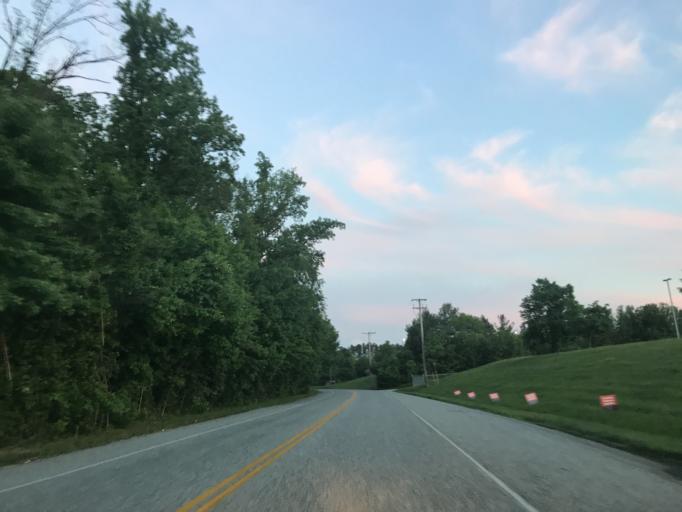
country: US
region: Maryland
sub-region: Harford County
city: Joppatowne
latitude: 39.4471
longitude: -76.3206
